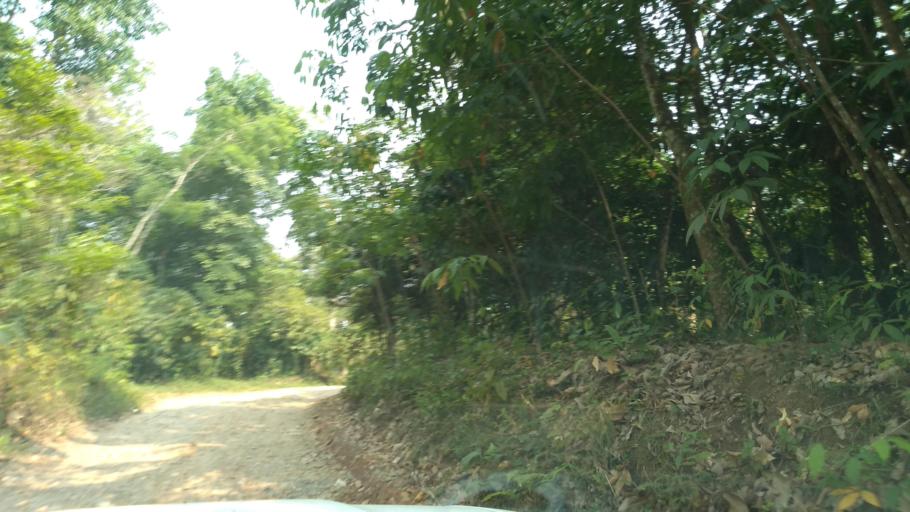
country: MX
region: Veracruz
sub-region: Tezonapa
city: Laguna Chica (Pueblo Nuevo)
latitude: 18.5506
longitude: -96.7829
